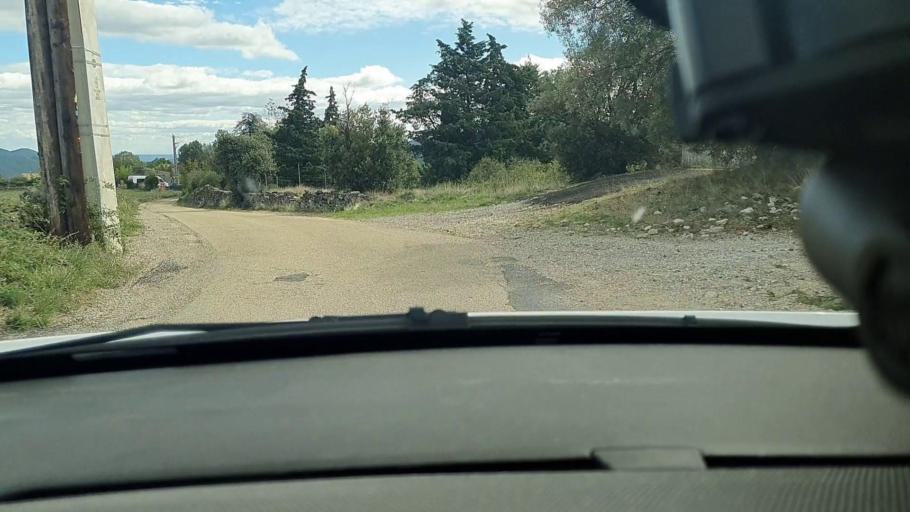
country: FR
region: Languedoc-Roussillon
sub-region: Departement du Gard
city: Besseges
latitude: 44.3084
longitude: 4.0254
